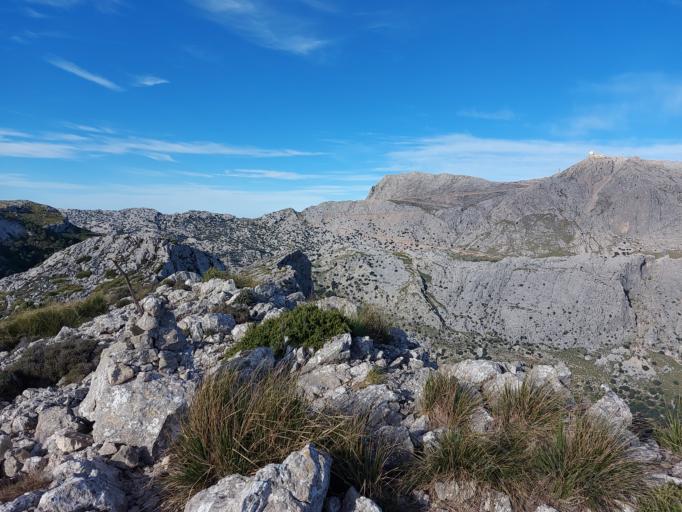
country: ES
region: Balearic Islands
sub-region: Illes Balears
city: Escorca
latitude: 39.7893
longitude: 2.8187
